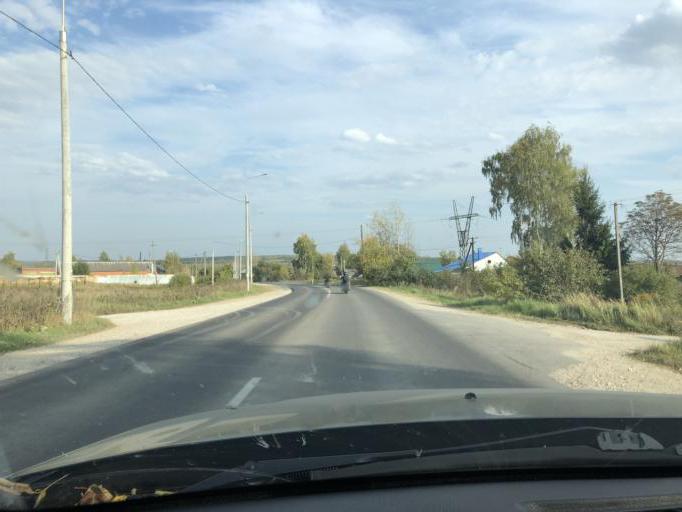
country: RU
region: Tula
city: Leninskiy
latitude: 54.2961
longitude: 37.4525
